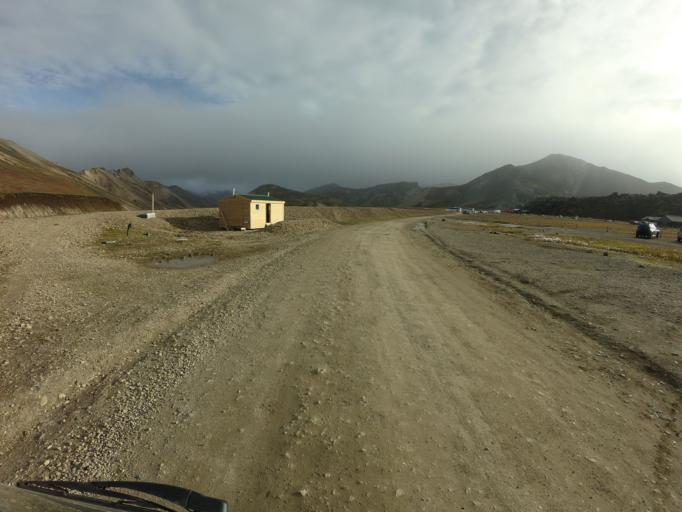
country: IS
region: South
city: Vestmannaeyjar
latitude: 63.9920
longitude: -19.0579
